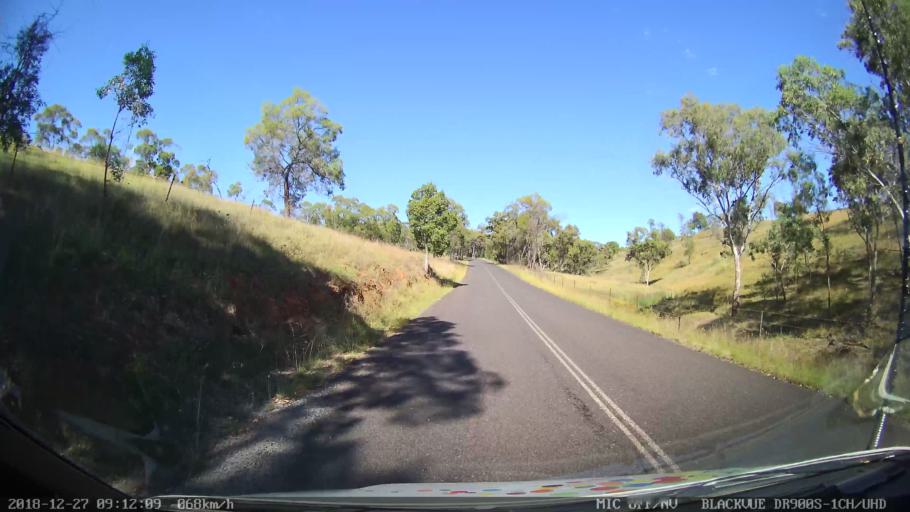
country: AU
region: New South Wales
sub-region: Lithgow
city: Portland
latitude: -33.1389
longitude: 150.1076
